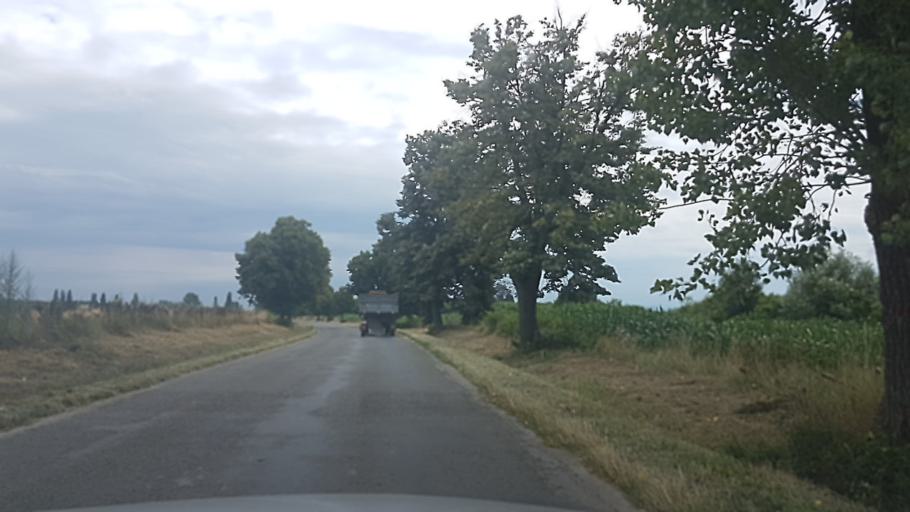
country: HU
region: Somogy
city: Barcs
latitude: 45.9593
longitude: 17.5961
